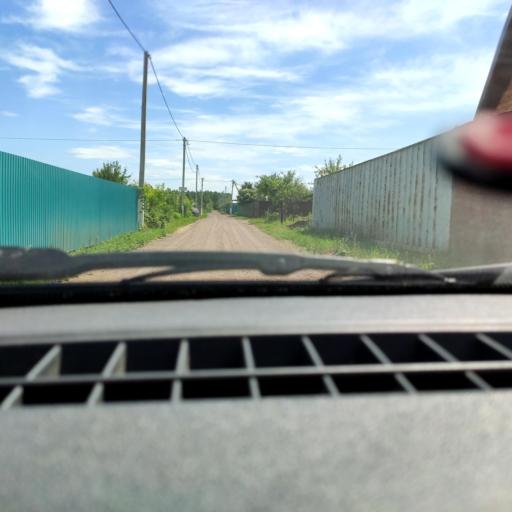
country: RU
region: Bashkortostan
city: Kabakovo
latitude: 54.7235
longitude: 56.2108
